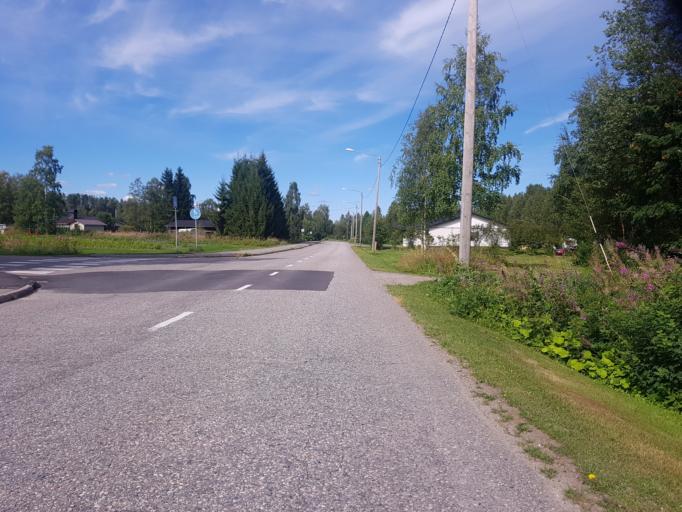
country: FI
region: Kainuu
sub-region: Kehys-Kainuu
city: Kuhmo
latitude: 64.1237
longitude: 29.5455
